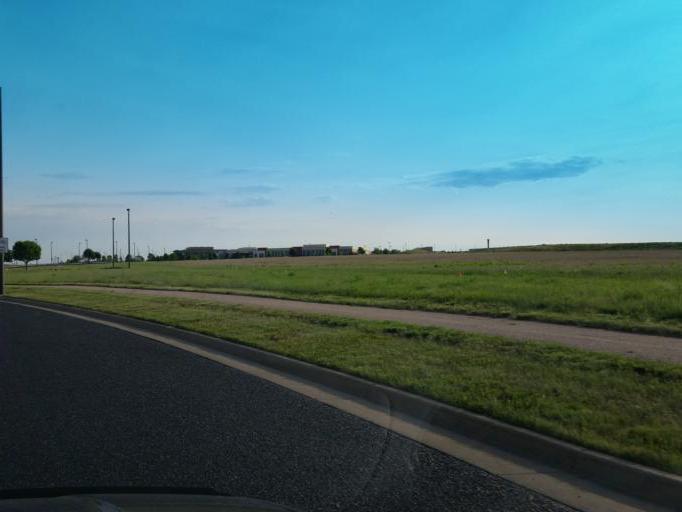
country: US
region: Colorado
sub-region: Larimer County
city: Loveland
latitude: 40.4248
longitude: -105.0018
